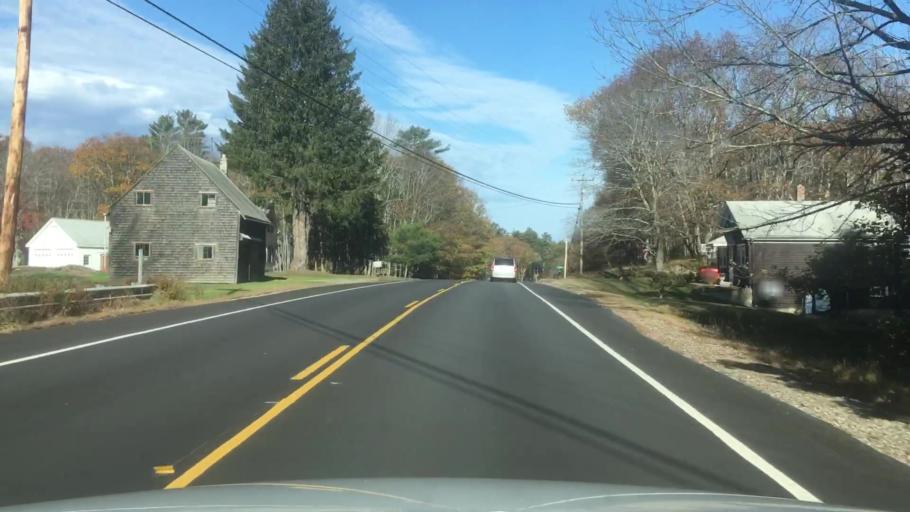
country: US
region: Maine
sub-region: Sagadahoc County
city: Woolwich
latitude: 43.8928
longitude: -69.7928
